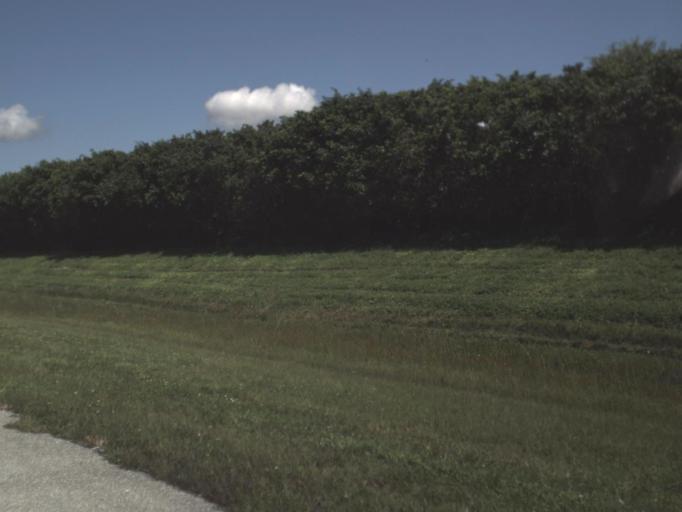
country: US
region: Florida
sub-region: Lee County
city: Pine Island Center
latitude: 26.6311
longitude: -82.0404
